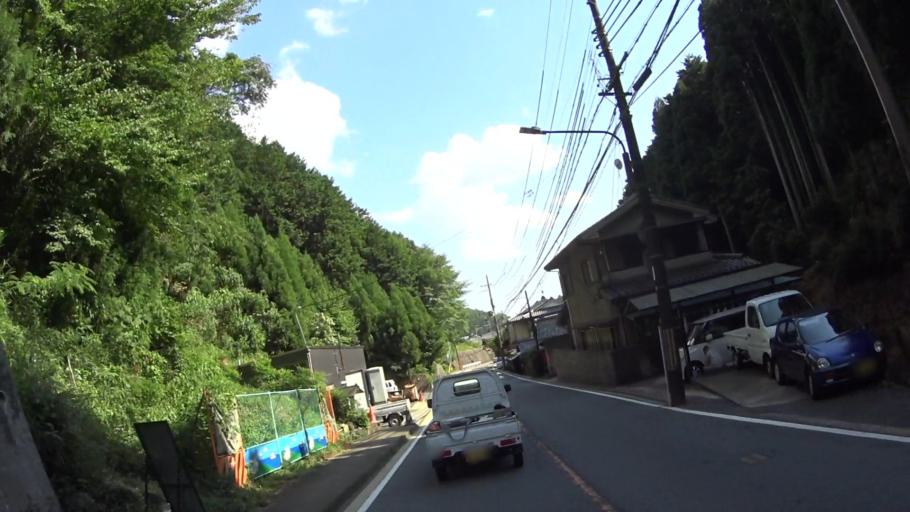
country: JP
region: Kyoto
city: Kyoto
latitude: 35.0440
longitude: 135.6854
